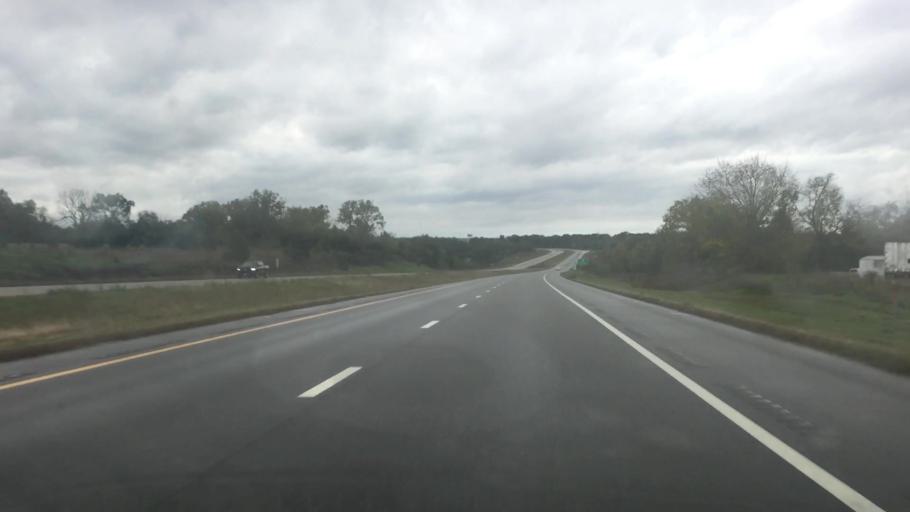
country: US
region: Kansas
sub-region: Miami County
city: Osawatomie
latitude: 38.5191
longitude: -94.9132
